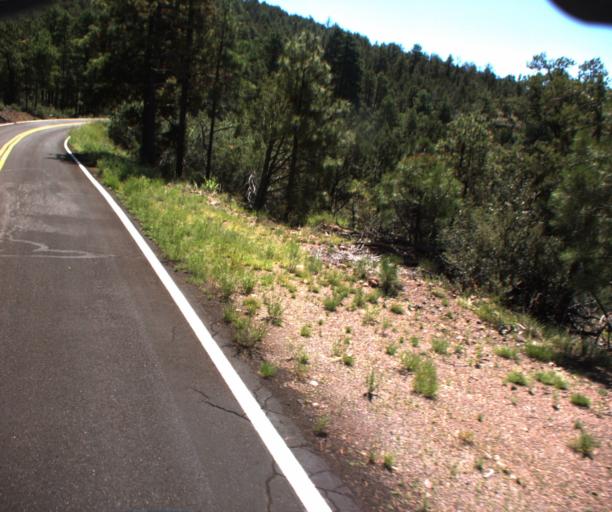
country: US
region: Arizona
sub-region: Greenlee County
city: Morenci
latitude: 33.4173
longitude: -109.3704
